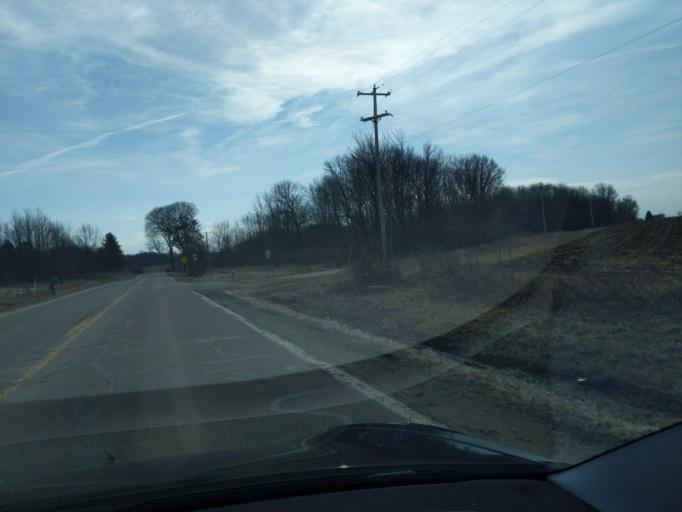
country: US
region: Michigan
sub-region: Ingham County
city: Stockbridge
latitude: 42.4940
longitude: -84.1040
